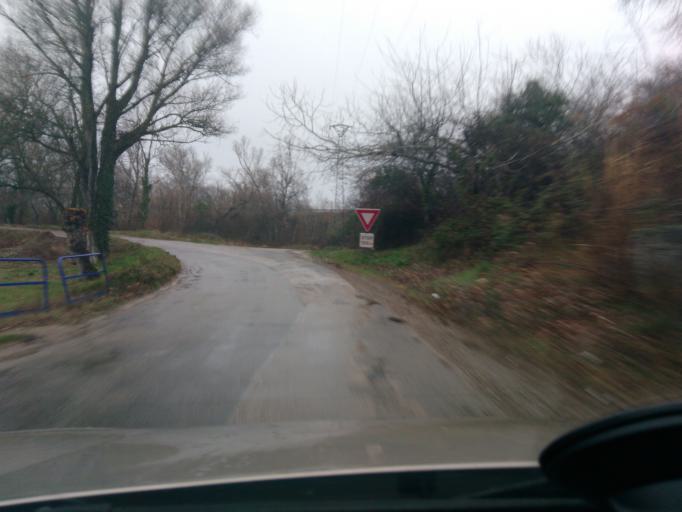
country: FR
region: Rhone-Alpes
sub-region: Departement de la Drome
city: Ancone
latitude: 44.5533
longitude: 4.7130
